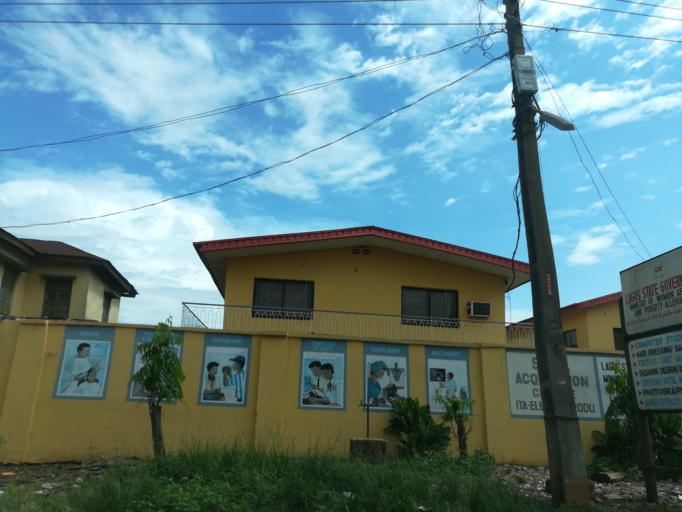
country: NG
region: Lagos
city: Ikorodu
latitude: 6.6127
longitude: 3.5070
